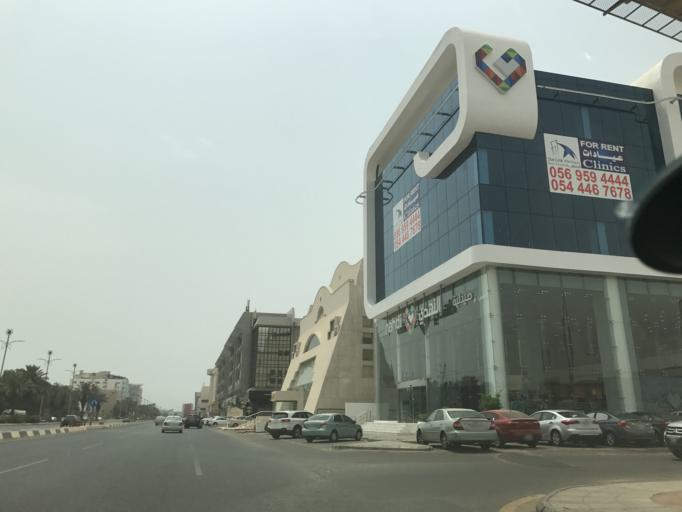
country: SA
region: Makkah
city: Jeddah
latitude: 21.5529
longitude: 39.1624
